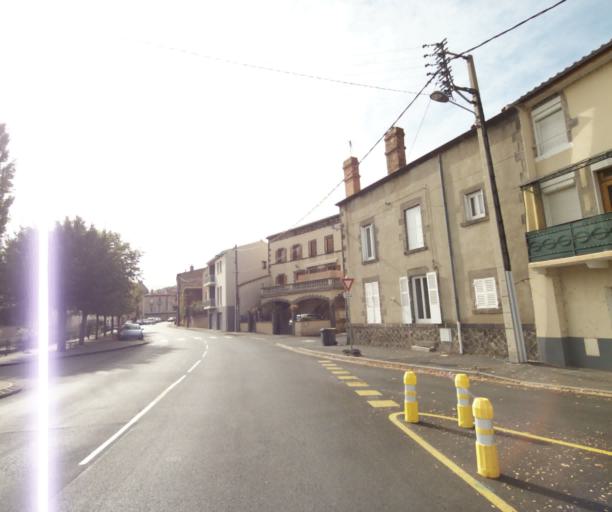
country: FR
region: Auvergne
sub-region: Departement du Puy-de-Dome
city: Aubiere
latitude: 45.7512
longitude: 3.1153
